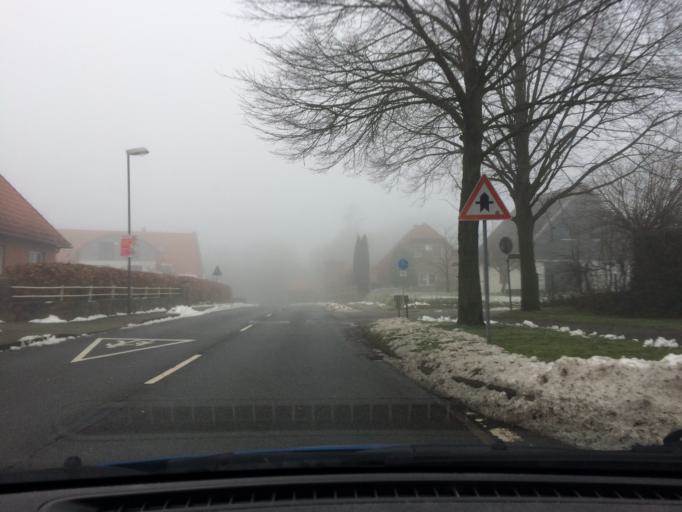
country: DE
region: Schleswig-Holstein
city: Gulzow
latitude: 53.4414
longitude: 10.4908
